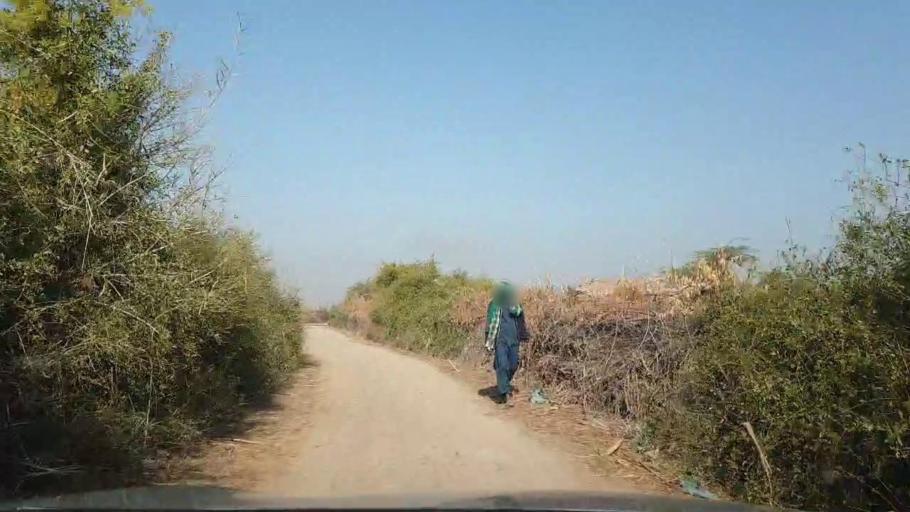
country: PK
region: Sindh
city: Mirpur Khas
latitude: 25.6476
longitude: 68.9101
